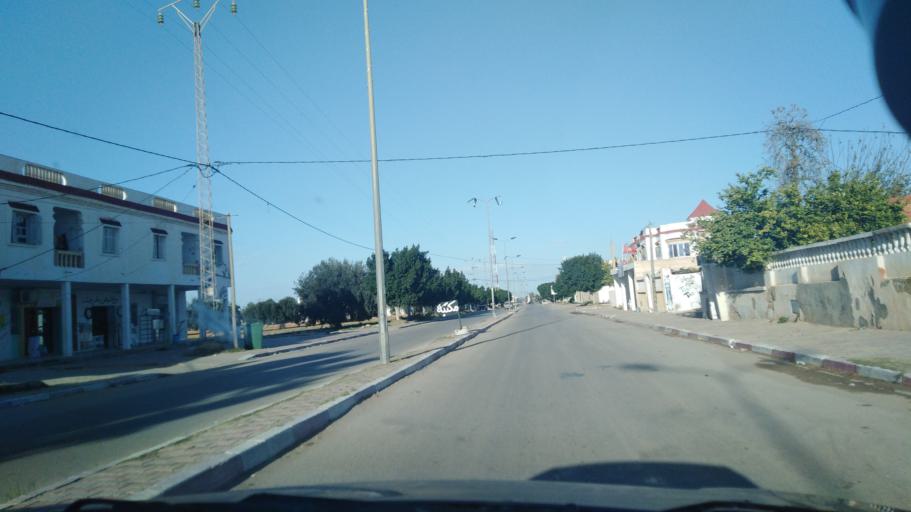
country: TN
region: Al Mahdiyah
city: Shurban
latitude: 34.9674
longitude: 10.3691
